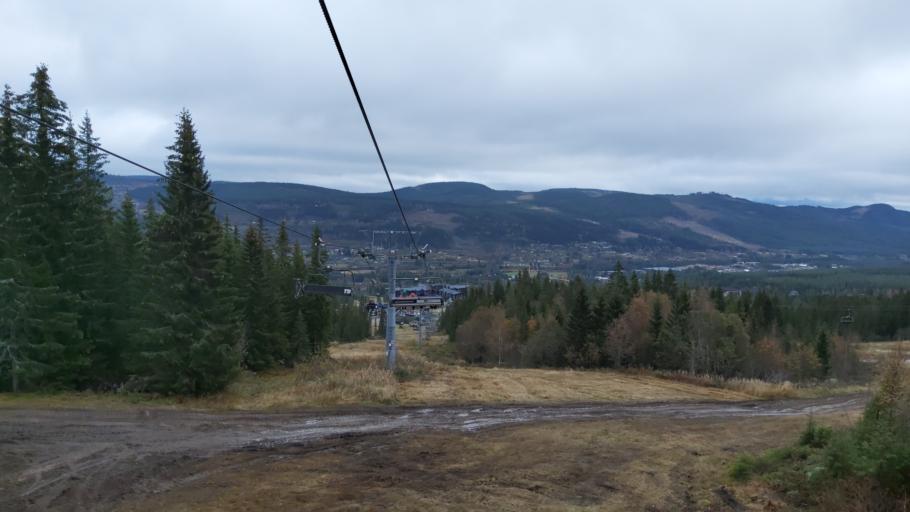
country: NO
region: Hedmark
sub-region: Trysil
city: Innbygda
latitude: 61.3082
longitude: 12.2263
